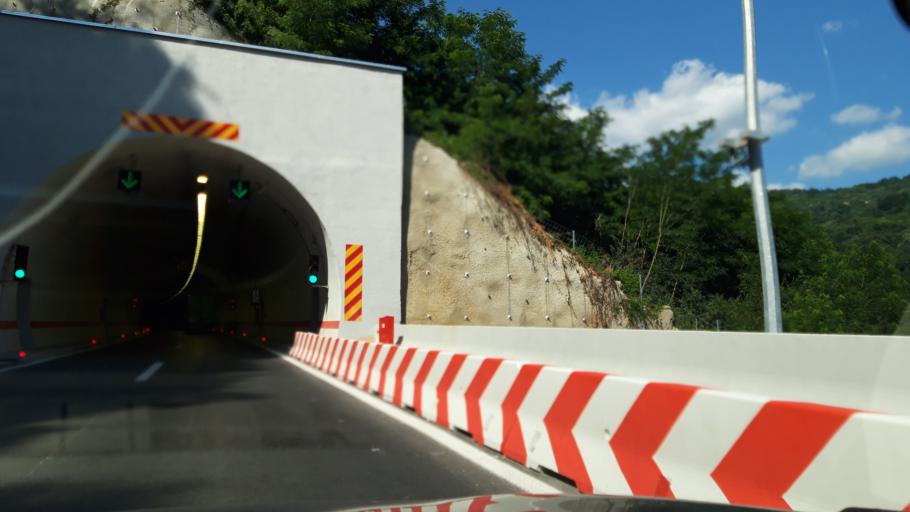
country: RS
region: Central Serbia
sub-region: Jablanicki Okrug
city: Vlasotince
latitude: 42.8356
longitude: 22.1300
